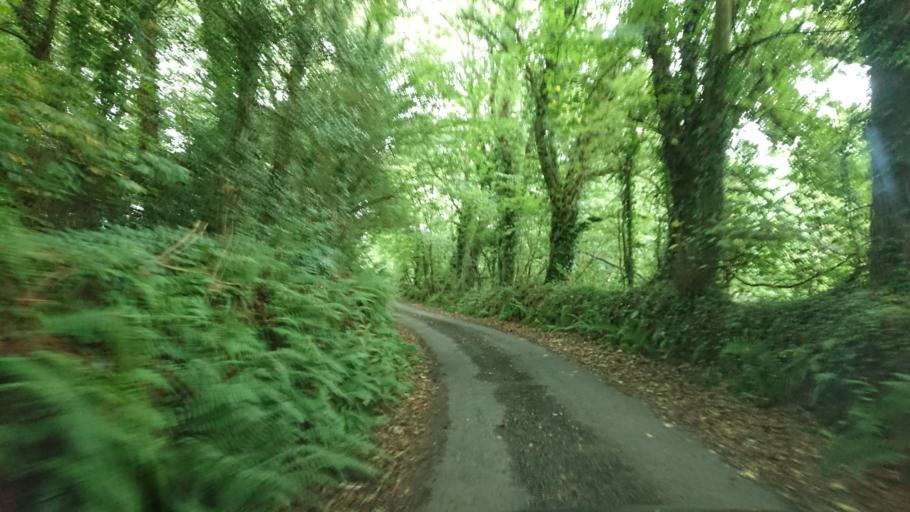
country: IE
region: Munster
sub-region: Waterford
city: Dunmore East
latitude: 52.1969
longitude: -7.0394
